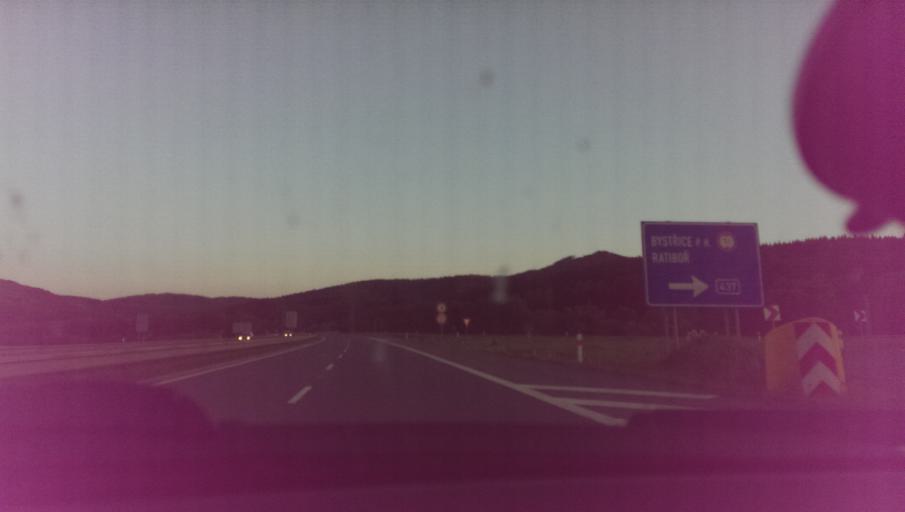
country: CZ
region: Zlin
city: Jablunka
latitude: 49.3727
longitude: 17.9435
